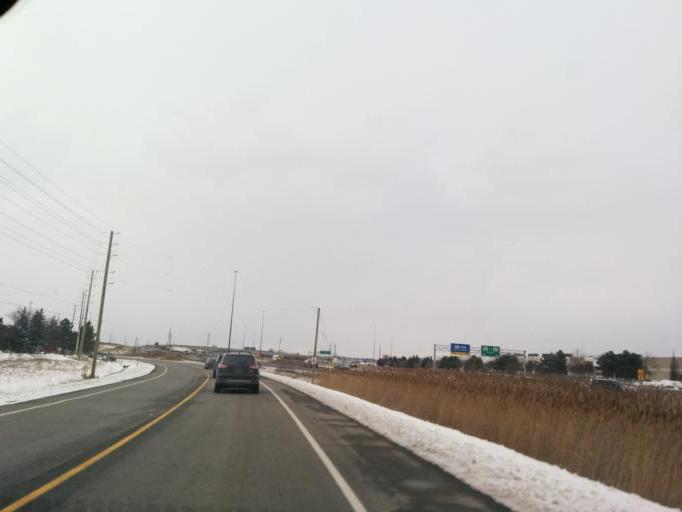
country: CA
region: Ontario
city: Oakville
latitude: 43.5230
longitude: -79.7172
